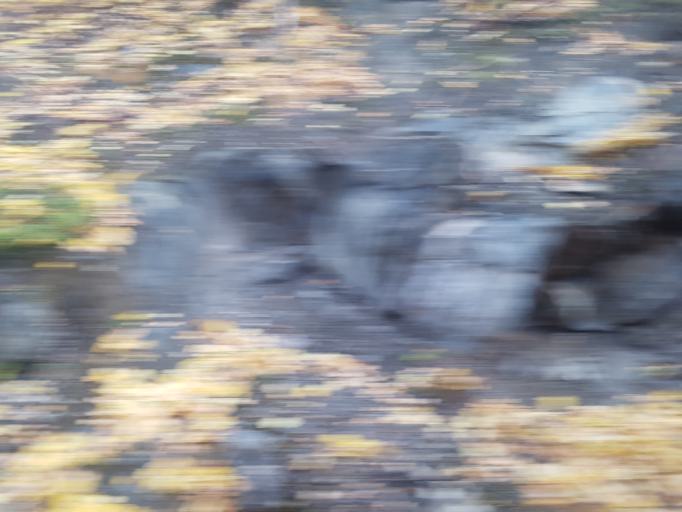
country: NO
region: Oppland
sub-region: Dovre
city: Dombas
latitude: 62.0475
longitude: 9.1478
